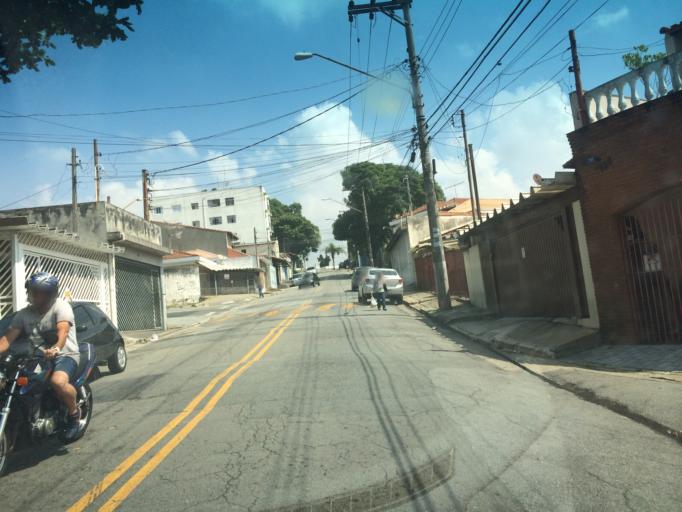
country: BR
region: Sao Paulo
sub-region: Guarulhos
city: Guarulhos
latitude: -23.4535
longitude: -46.5386
